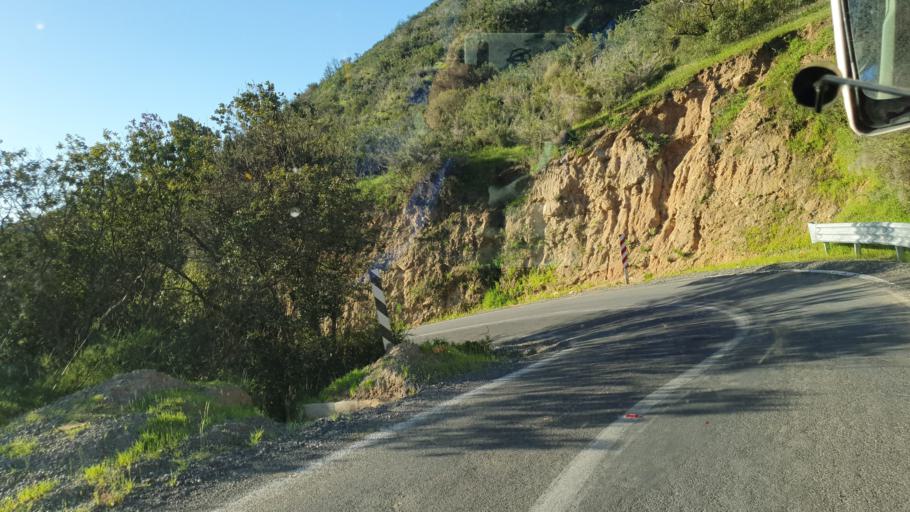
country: CL
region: Valparaiso
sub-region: Provincia de Marga Marga
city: Limache
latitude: -33.1957
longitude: -71.2739
